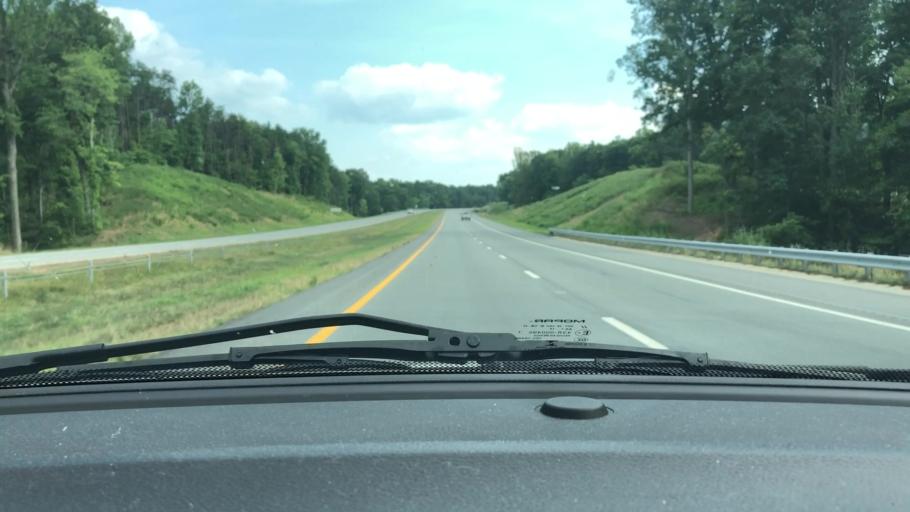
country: US
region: North Carolina
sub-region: Guilford County
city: Oak Ridge
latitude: 36.1512
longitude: -79.9592
